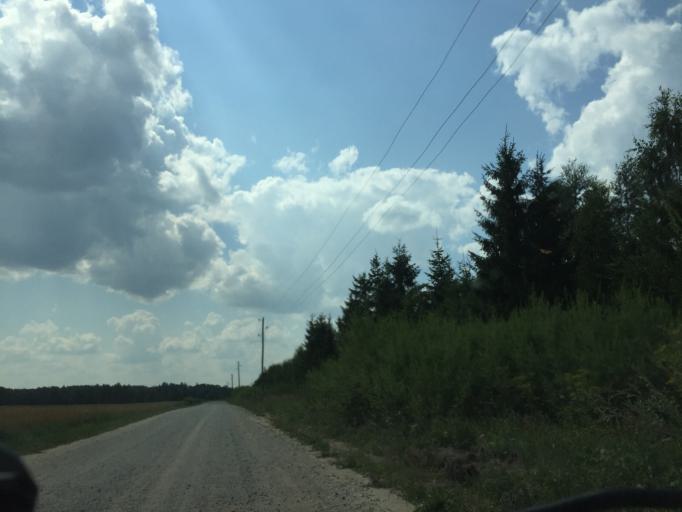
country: LT
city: Zagare
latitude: 56.3819
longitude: 23.1778
